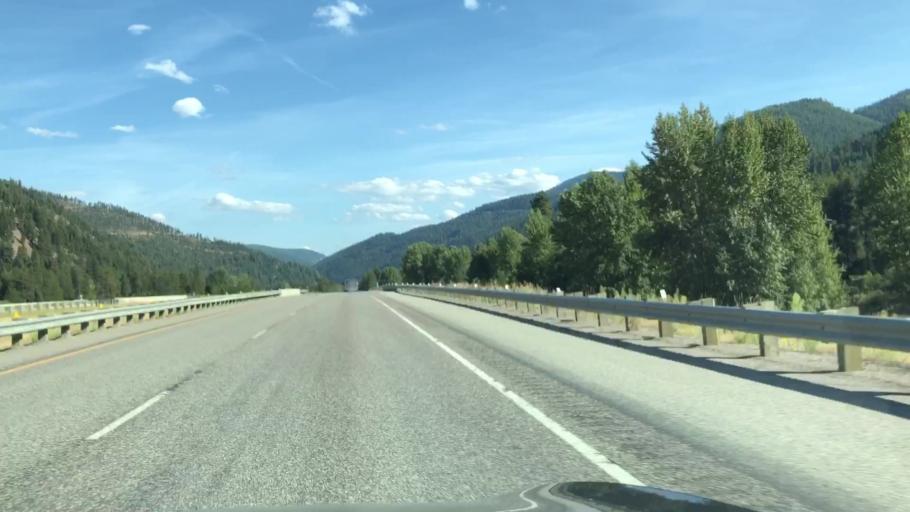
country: US
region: Montana
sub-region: Sanders County
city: Thompson Falls
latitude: 47.3762
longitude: -115.3513
